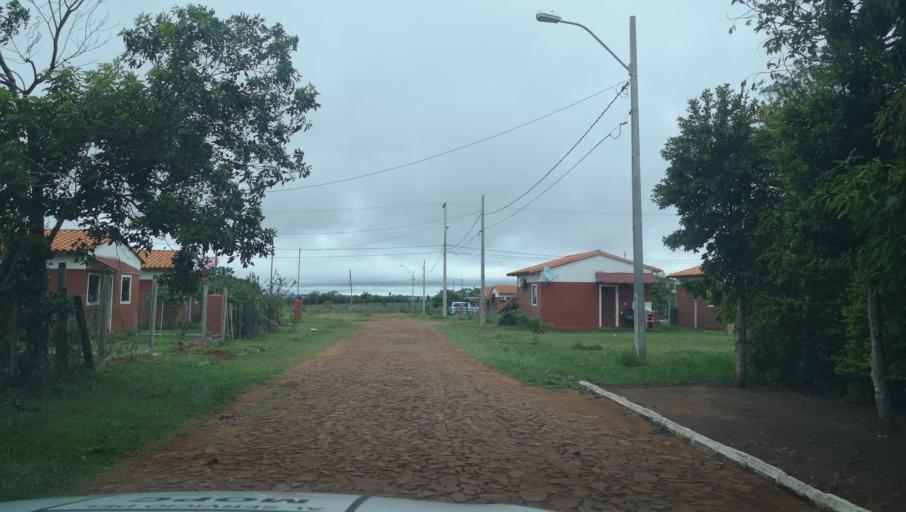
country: PY
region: Misiones
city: Santa Maria
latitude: -26.9016
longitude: -57.0370
